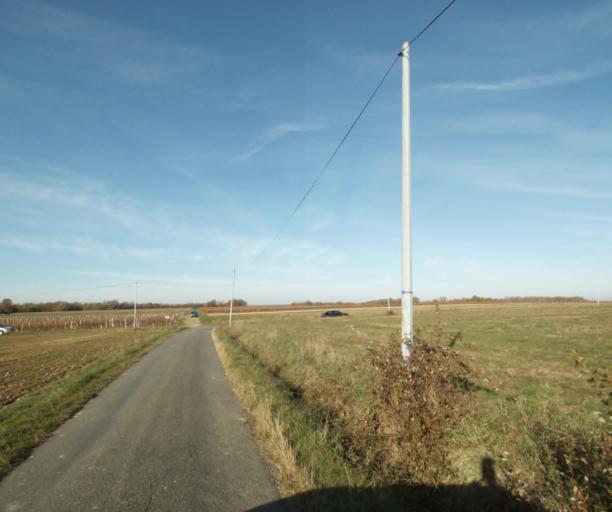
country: FR
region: Poitou-Charentes
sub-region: Departement de la Charente-Maritime
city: Cherac
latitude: 45.7473
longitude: -0.4849
